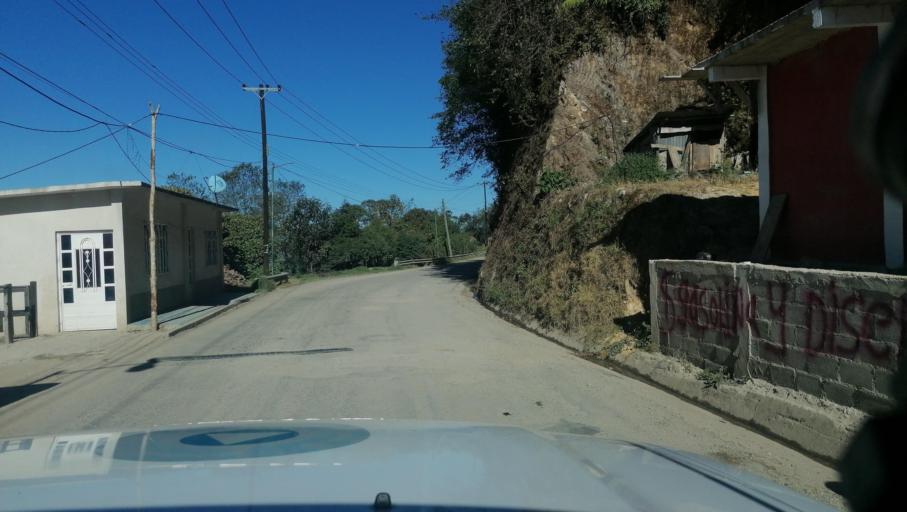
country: MX
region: Chiapas
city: Motozintla de Mendoza
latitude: 15.2606
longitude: -92.2140
